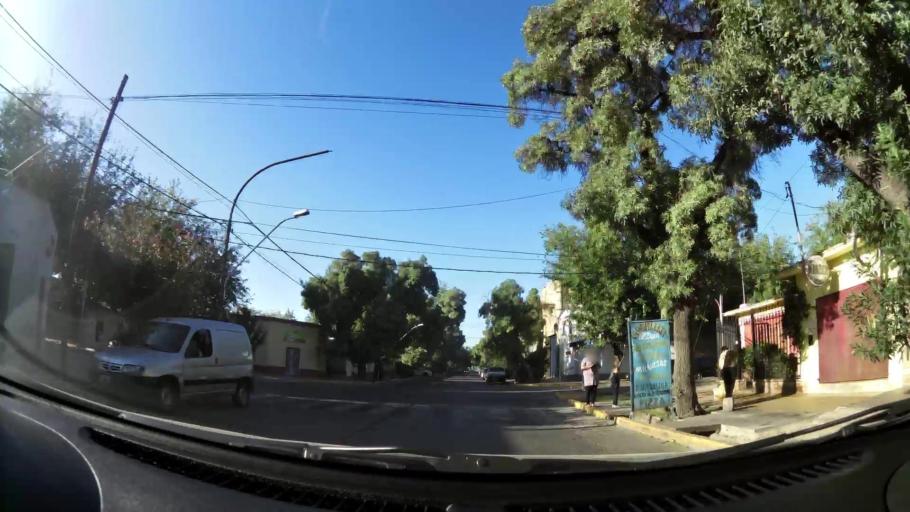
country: AR
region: Mendoza
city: Las Heras
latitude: -32.8694
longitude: -68.8230
